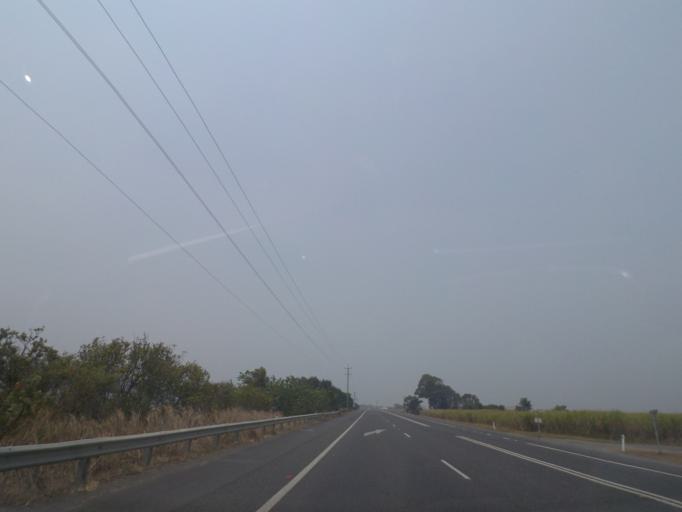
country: AU
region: New South Wales
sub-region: Richmond Valley
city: Evans Head
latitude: -28.9968
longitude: 153.4522
